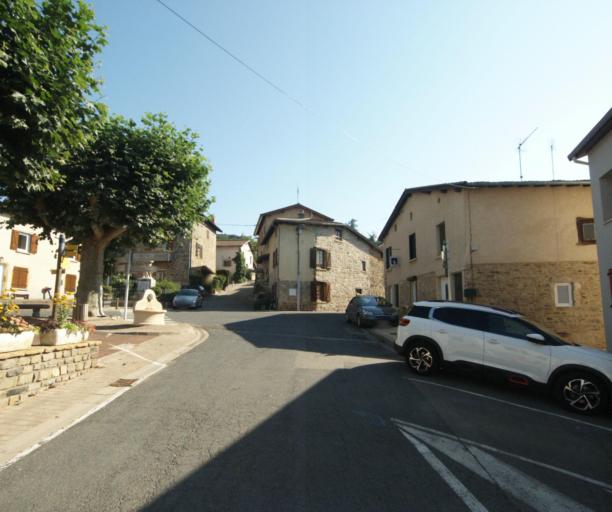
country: FR
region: Rhone-Alpes
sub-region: Departement du Rhone
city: Saint-Pierre-la-Palud
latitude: 45.7706
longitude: 4.6076
